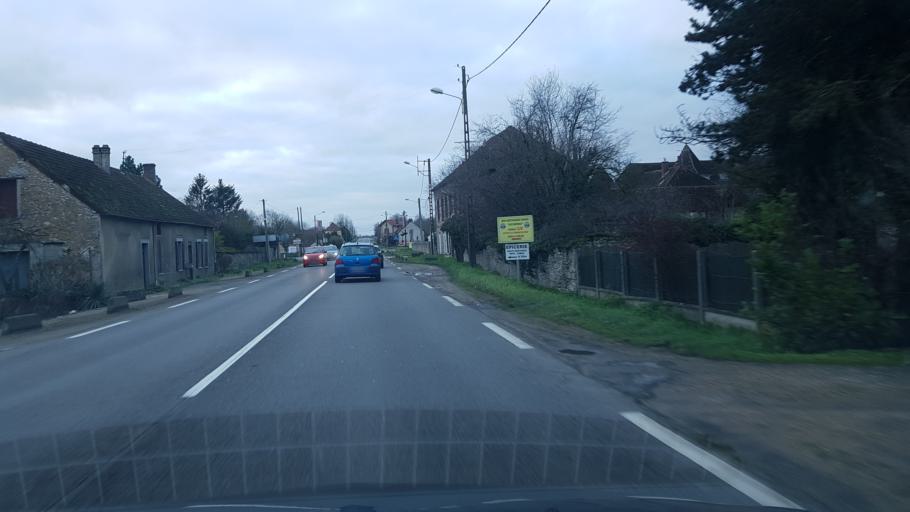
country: FR
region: Champagne-Ardenne
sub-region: Departement de la Marne
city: Esternay
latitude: 48.7138
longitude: 3.4889
